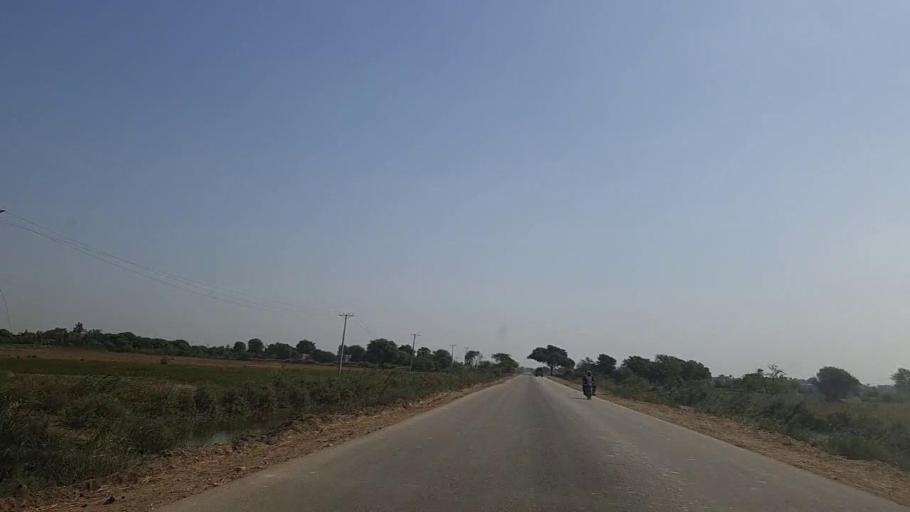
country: PK
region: Sindh
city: Daro Mehar
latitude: 24.7762
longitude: 68.2037
